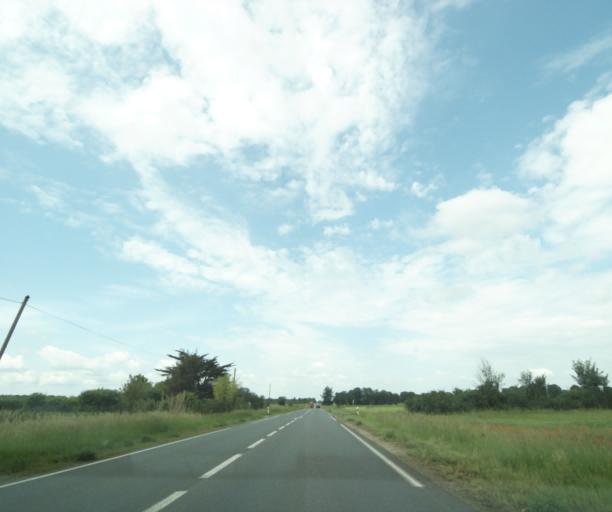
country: FR
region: Pays de la Loire
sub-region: Departement de Maine-et-Loire
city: Montreuil-Bellay
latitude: 47.1465
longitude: -0.1512
